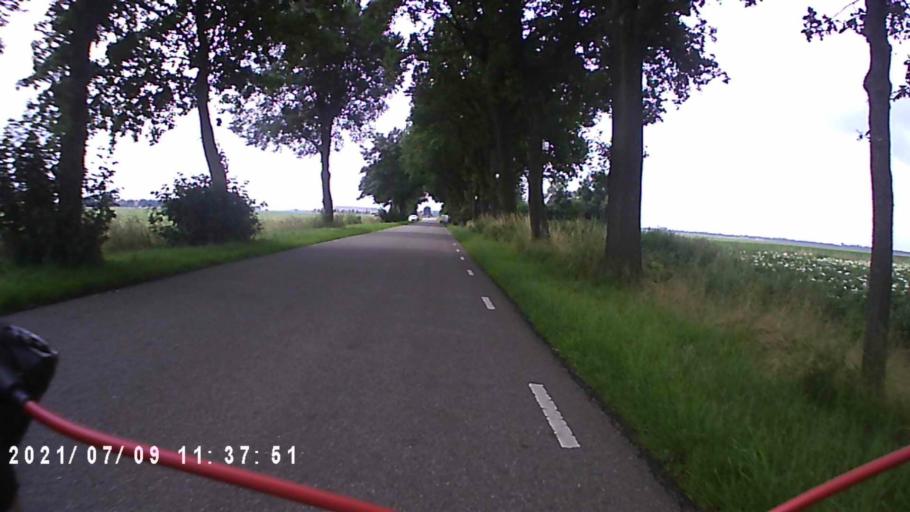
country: NL
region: Groningen
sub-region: Gemeente Slochteren
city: Slochteren
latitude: 53.2240
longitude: 6.8723
